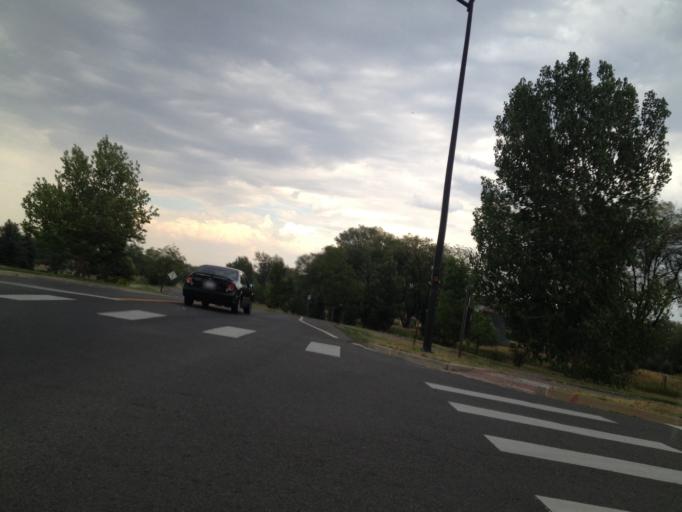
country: US
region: Colorado
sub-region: Boulder County
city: Louisville
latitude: 39.9699
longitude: -105.1327
